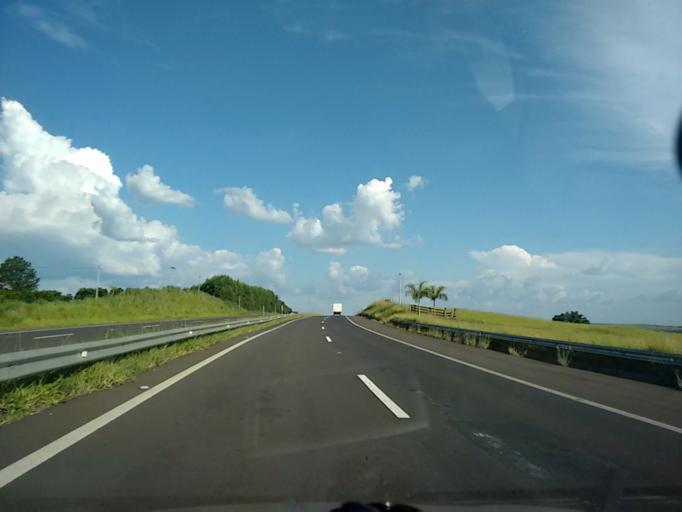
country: BR
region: Sao Paulo
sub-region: Garca
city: Garca
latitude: -22.2681
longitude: -49.5103
